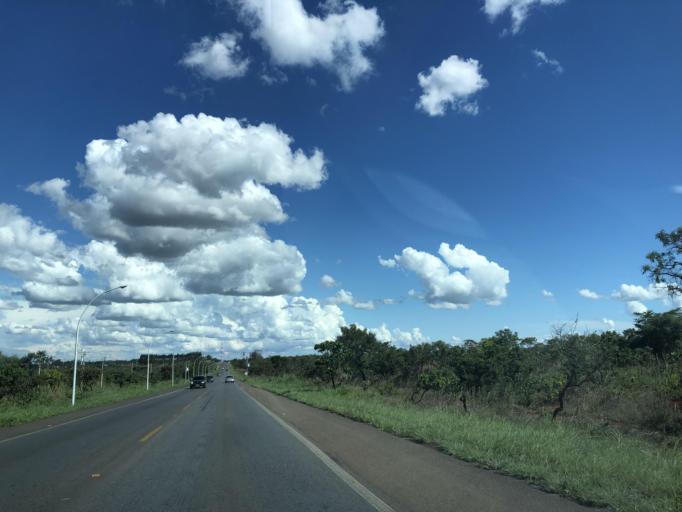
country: BR
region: Federal District
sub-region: Brasilia
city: Brasilia
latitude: -15.6757
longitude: -47.8744
